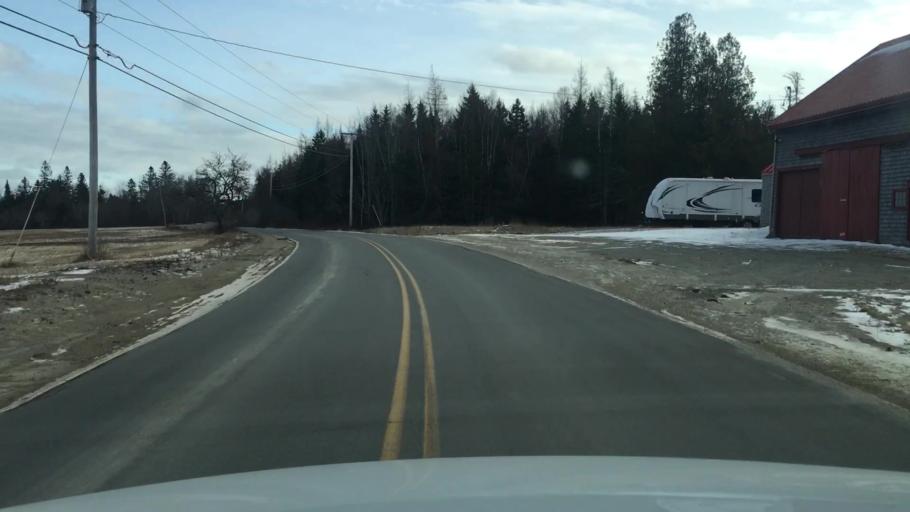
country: US
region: Maine
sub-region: Washington County
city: Jonesport
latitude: 44.6163
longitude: -67.6063
